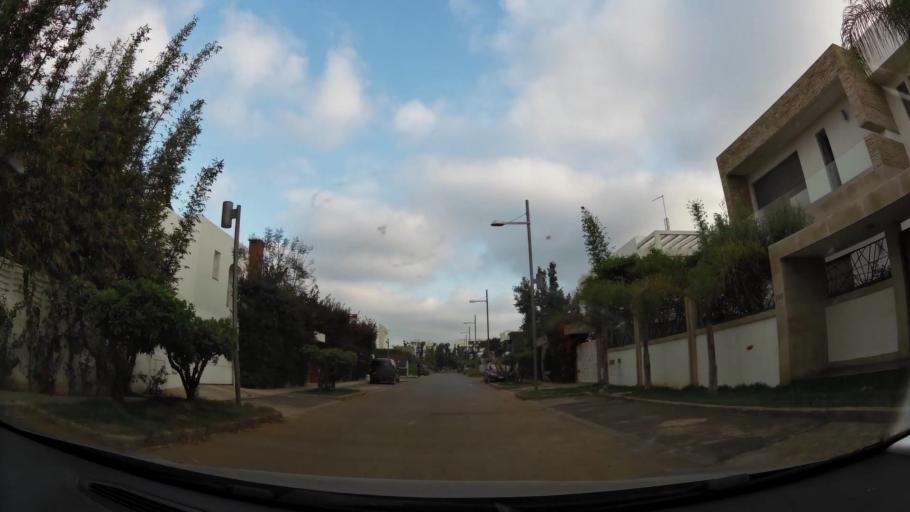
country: MA
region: Rabat-Sale-Zemmour-Zaer
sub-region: Rabat
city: Rabat
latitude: 33.9535
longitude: -6.8379
